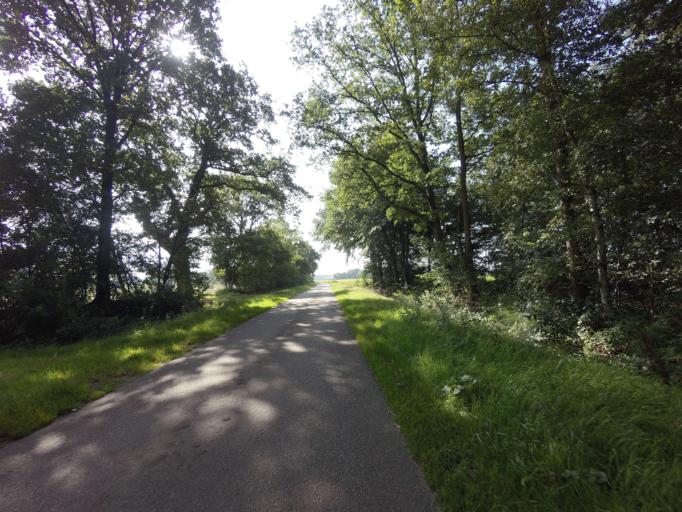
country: NL
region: Drenthe
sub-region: Gemeente Borger-Odoorn
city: Borger
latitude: 52.9358
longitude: 6.6976
